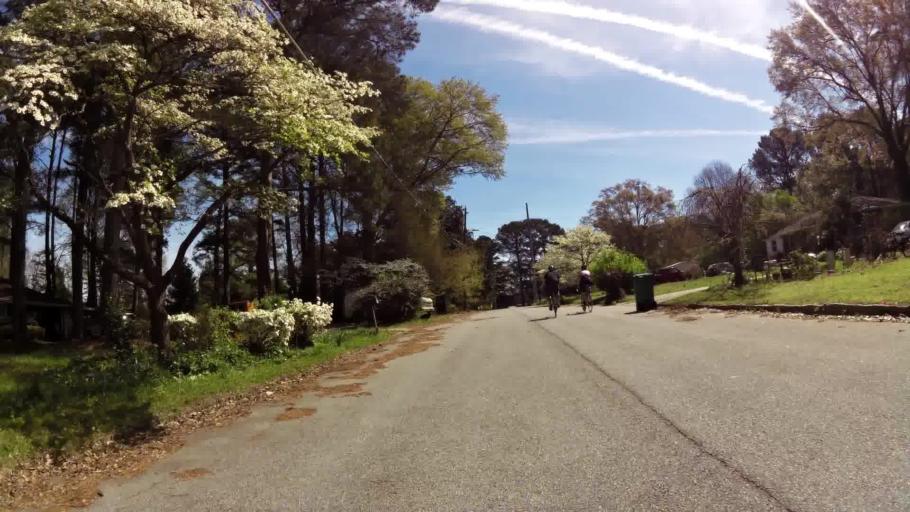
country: US
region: Georgia
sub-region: DeKalb County
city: Clarkston
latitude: 33.8410
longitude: -84.2580
